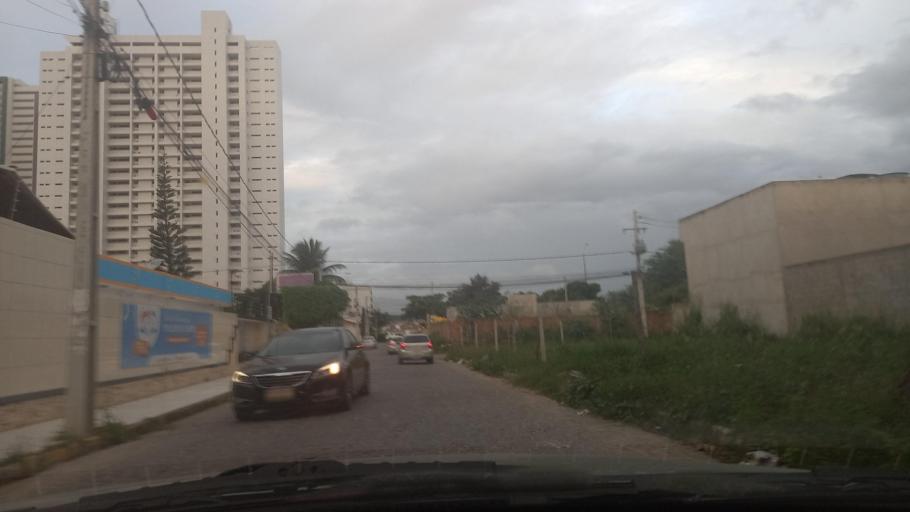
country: BR
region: Pernambuco
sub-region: Caruaru
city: Caruaru
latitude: -8.2667
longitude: -35.9655
